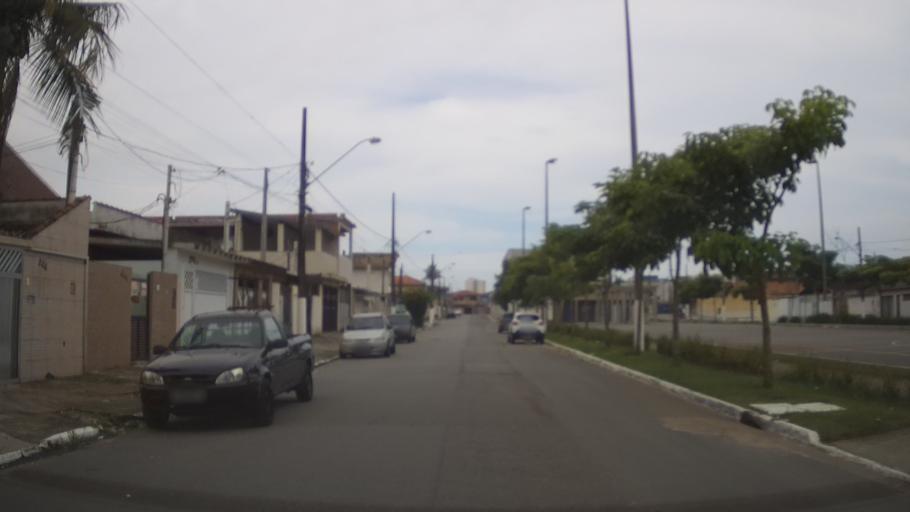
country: BR
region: Sao Paulo
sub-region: Praia Grande
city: Praia Grande
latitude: -24.0073
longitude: -46.4562
